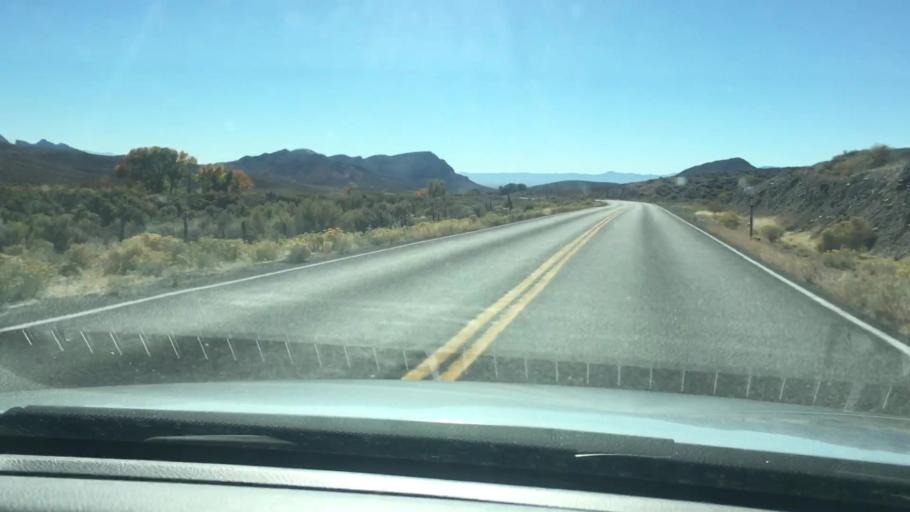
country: US
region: Nevada
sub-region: White Pine County
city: Ely
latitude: 38.7855
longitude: -115.4065
